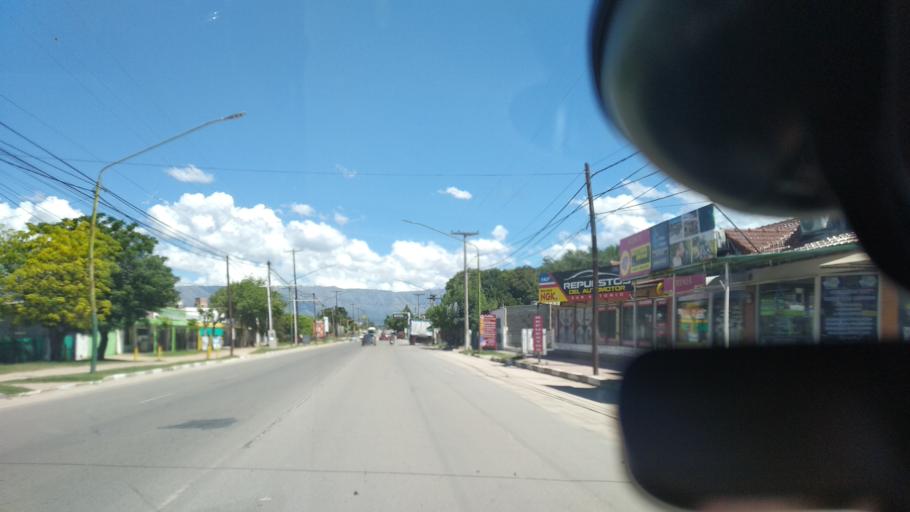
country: AR
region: Cordoba
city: Villa Cura Brochero
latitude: -31.7130
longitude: -65.0144
